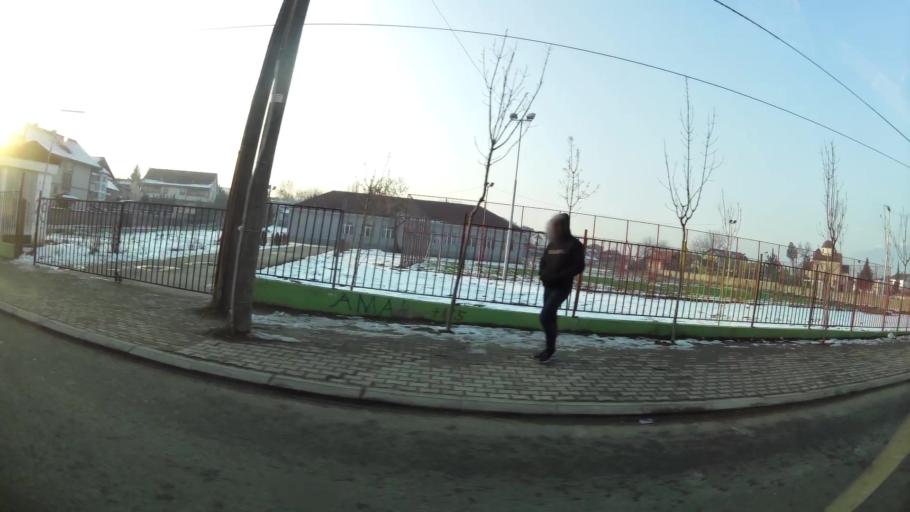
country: MK
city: Creshevo
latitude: 42.0152
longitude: 21.5115
